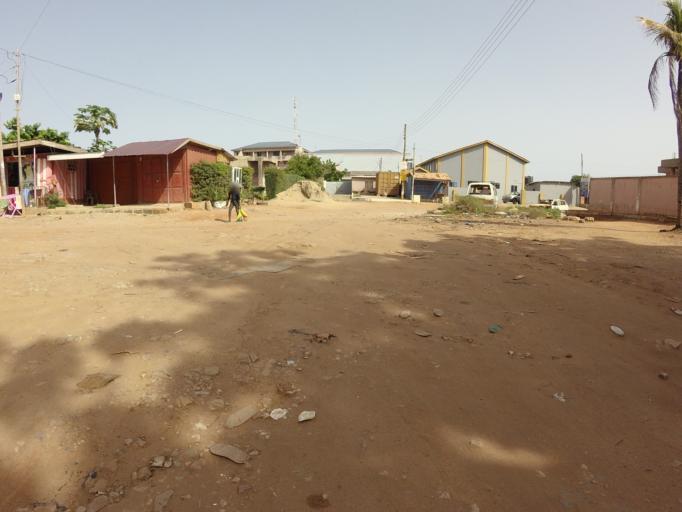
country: GH
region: Greater Accra
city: Dome
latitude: 5.6099
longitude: -0.2417
